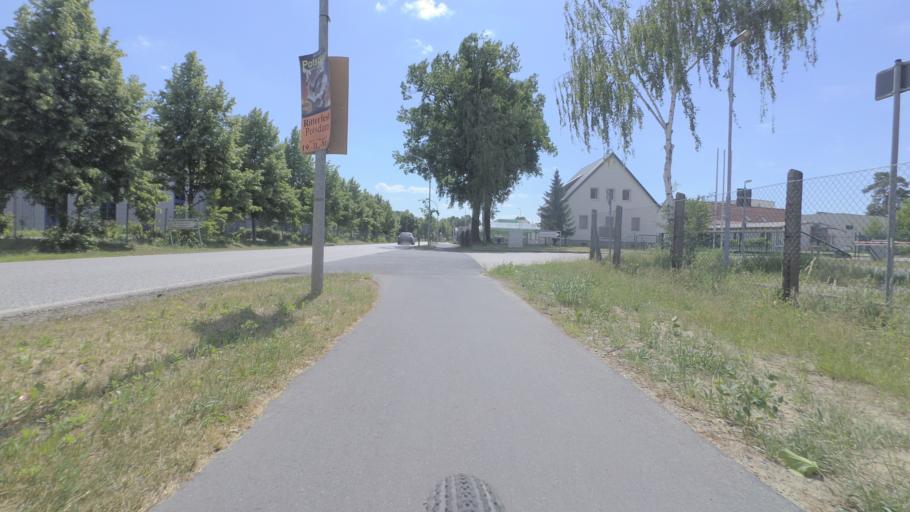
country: DE
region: Brandenburg
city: Ludwigsfelde
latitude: 52.3010
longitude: 13.2748
